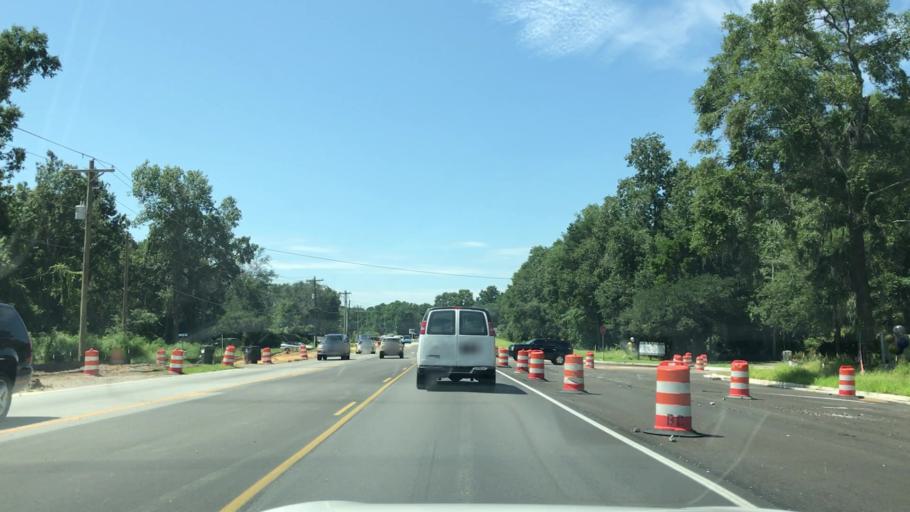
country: US
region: South Carolina
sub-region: Charleston County
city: North Charleston
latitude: 32.8899
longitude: -79.9275
